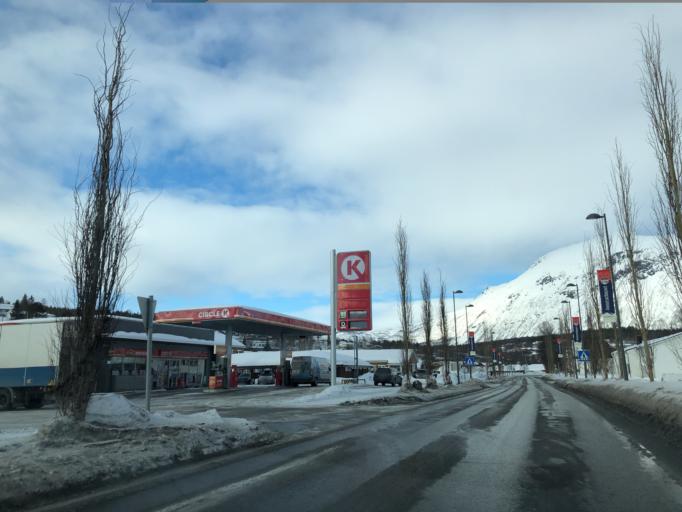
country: NO
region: Troms
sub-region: Bardu
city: Setermoen
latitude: 68.8630
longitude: 18.3473
